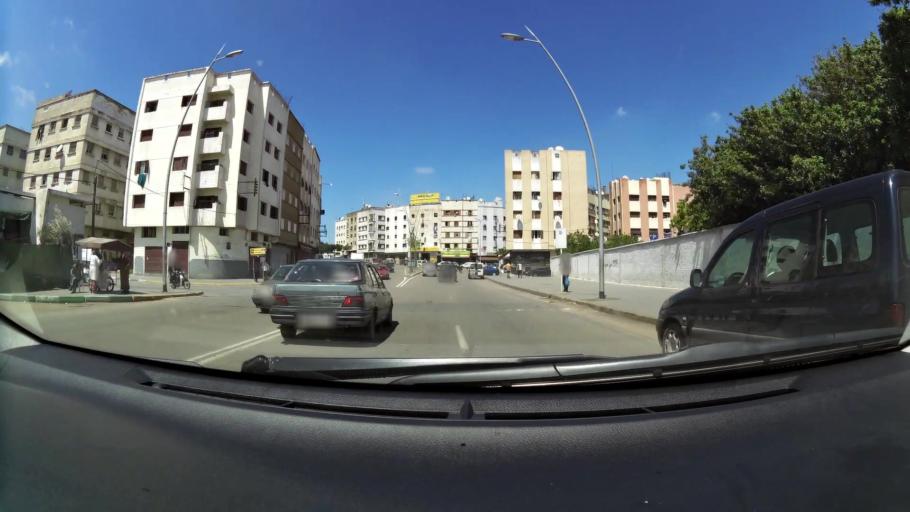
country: MA
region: Grand Casablanca
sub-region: Casablanca
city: Casablanca
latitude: 33.5636
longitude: -7.5876
